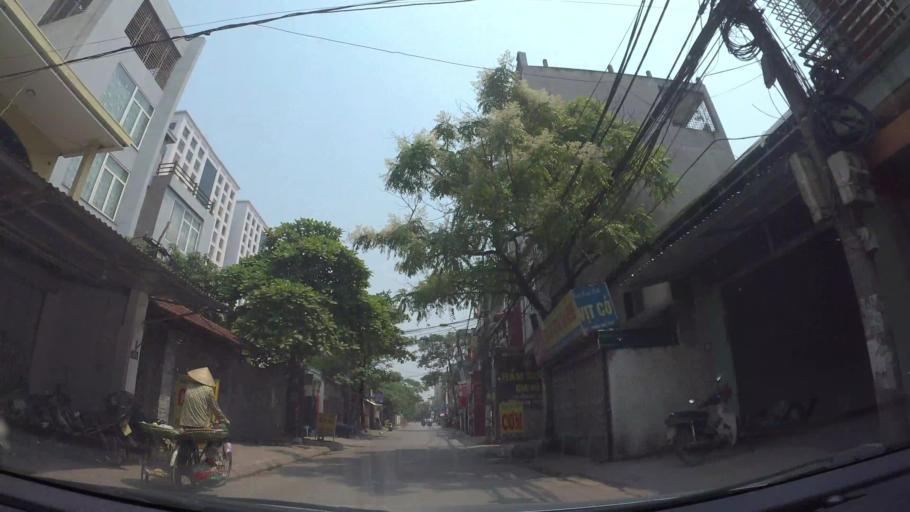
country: VN
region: Ha Noi
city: Thanh Xuan
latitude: 20.9969
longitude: 105.7880
